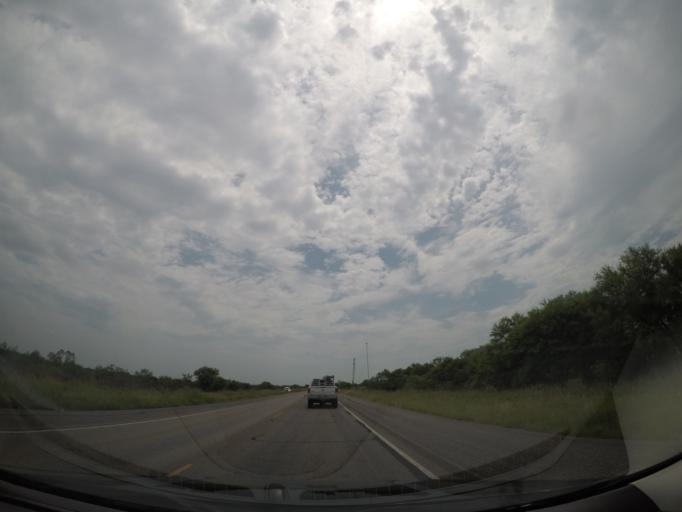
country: US
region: Texas
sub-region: Val Verde County
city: Laughlin Air Force Base
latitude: 29.3871
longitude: -100.7441
